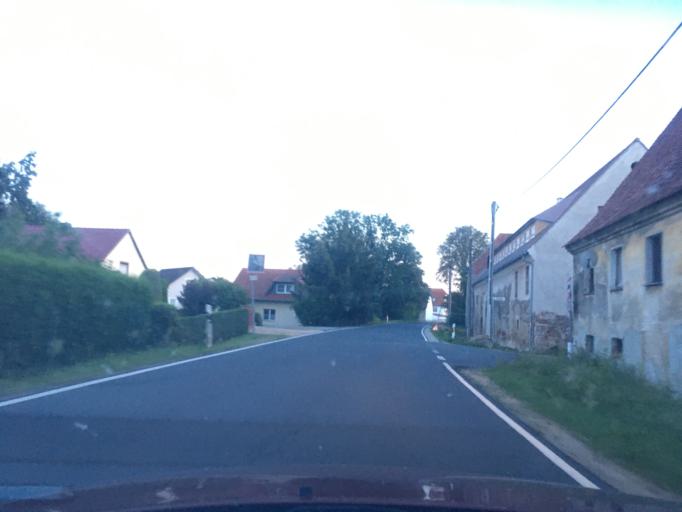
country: PL
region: Lower Silesian Voivodeship
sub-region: Powiat zgorzelecki
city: Piensk
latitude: 51.2191
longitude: 15.0046
